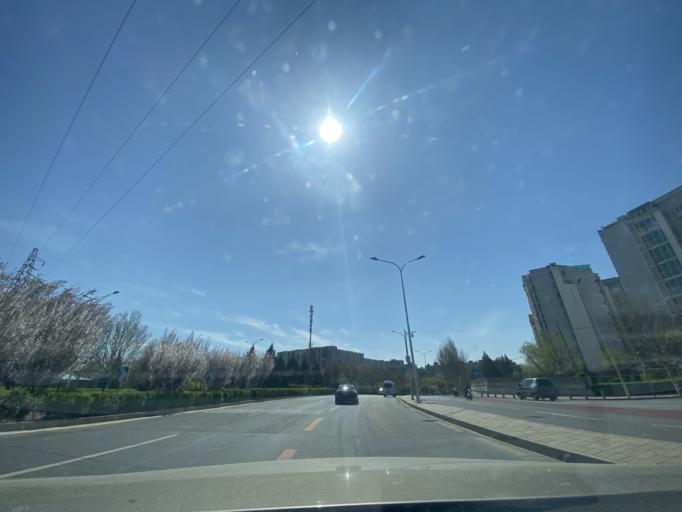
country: CN
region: Beijing
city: Sijiqing
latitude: 39.9334
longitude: 116.2463
